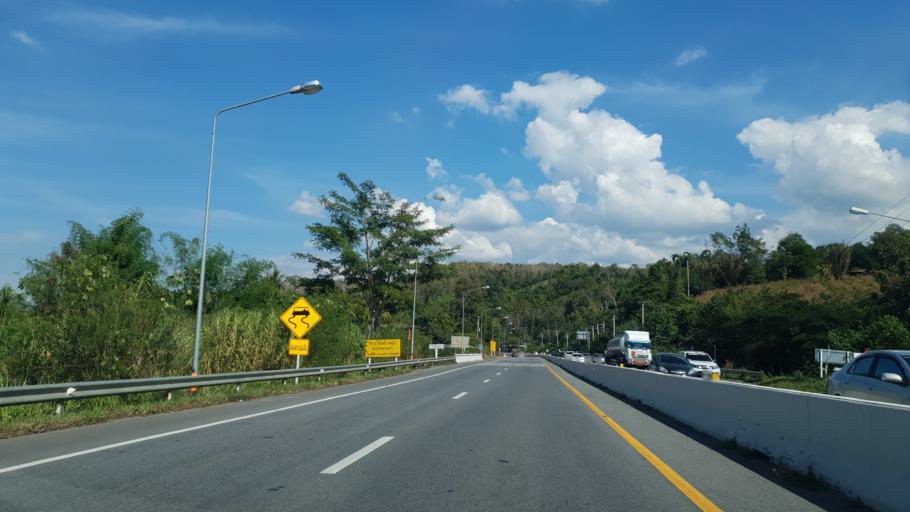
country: TH
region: Phrae
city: Den Chai
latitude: 17.9029
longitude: 100.0626
